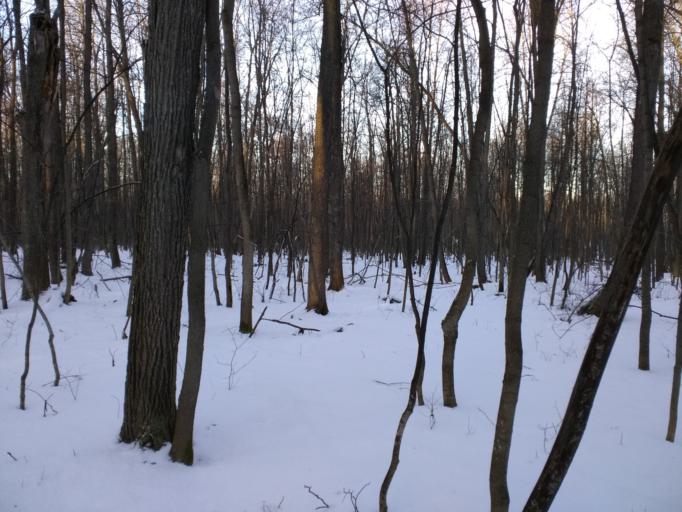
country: RU
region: Bashkortostan
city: Kudeyevskiy
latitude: 54.8041
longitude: 56.5926
